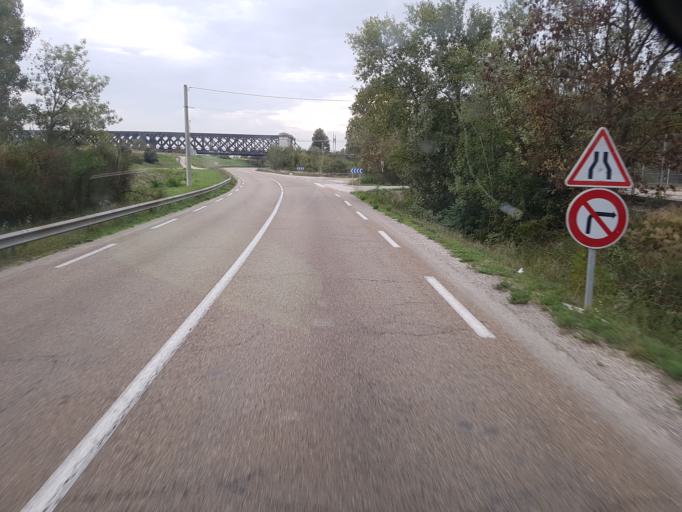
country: FR
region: Languedoc-Roussillon
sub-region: Departement du Gard
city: Les Angles
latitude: 43.9438
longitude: 4.7817
